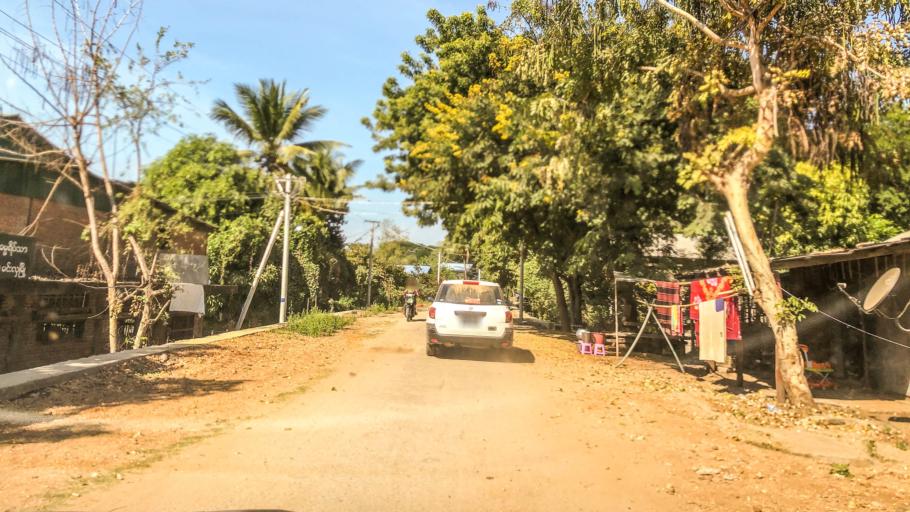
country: MM
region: Magway
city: Magway
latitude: 19.9709
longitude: 95.0425
